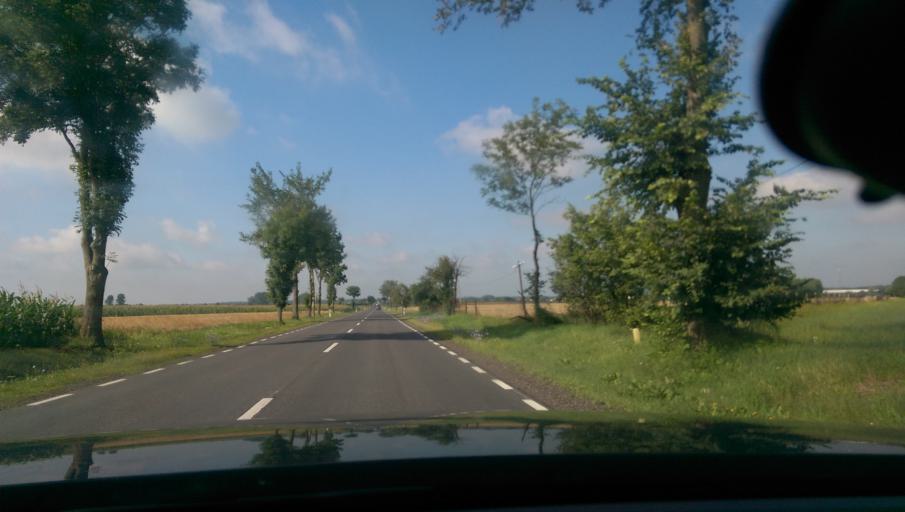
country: PL
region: Masovian Voivodeship
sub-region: Powiat plonski
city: Sochocin
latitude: 52.7020
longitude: 20.4866
